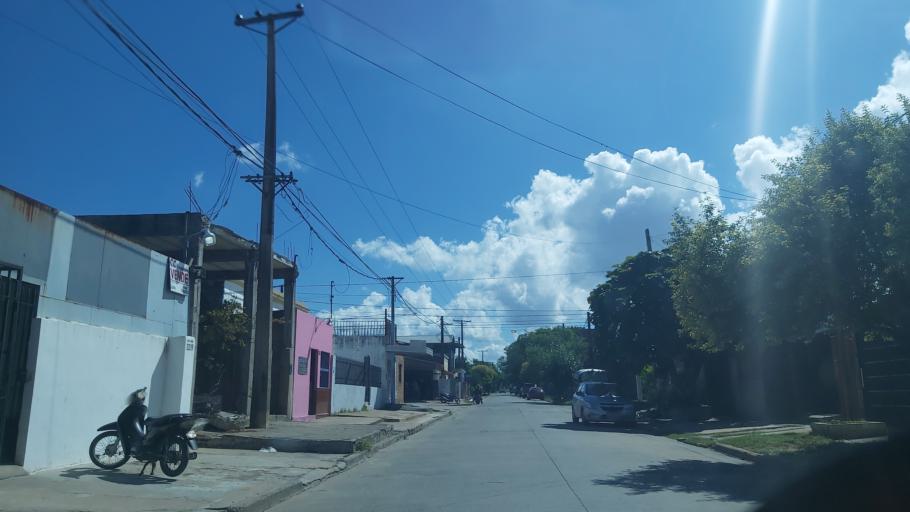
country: AR
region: Corrientes
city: Corrientes
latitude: -27.4819
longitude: -58.8492
